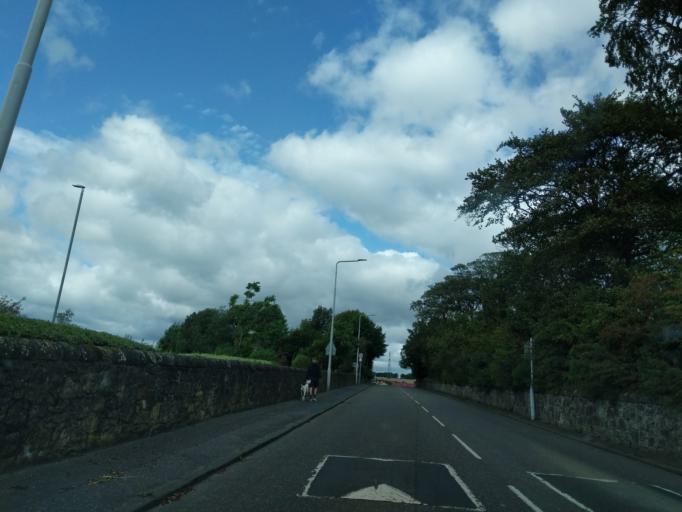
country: GB
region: Scotland
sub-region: Fife
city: Dunfermline
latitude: 56.0823
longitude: -3.4627
